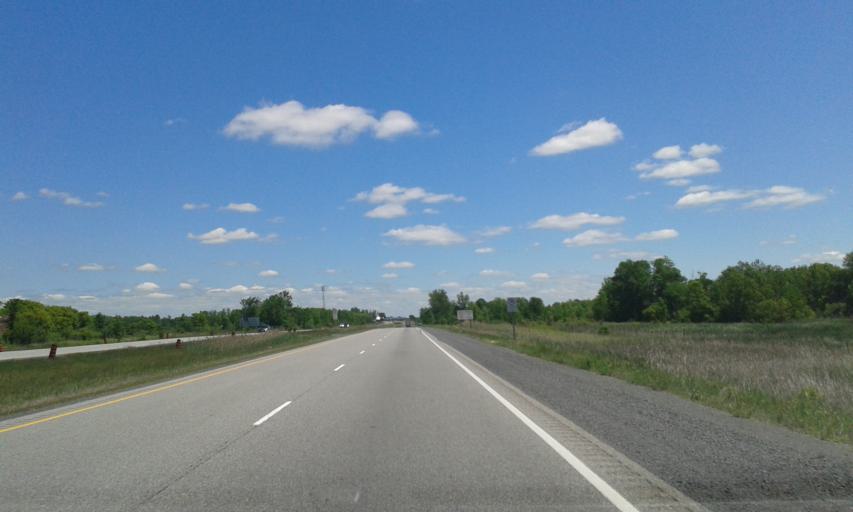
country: US
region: New York
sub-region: St. Lawrence County
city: Norfolk
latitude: 44.9564
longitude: -75.1015
